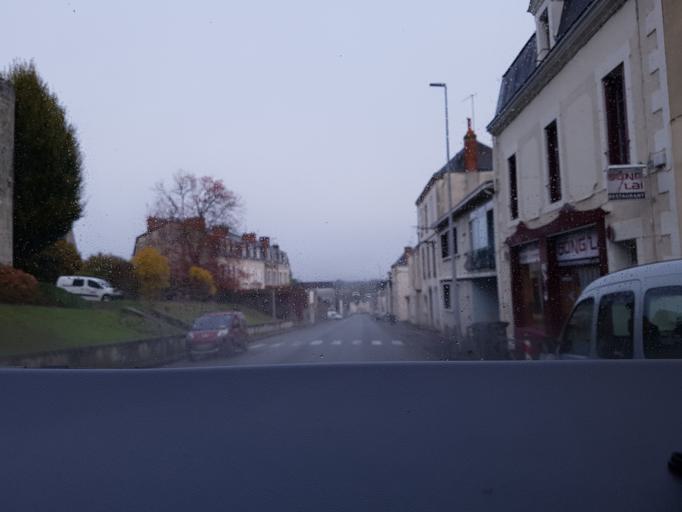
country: FR
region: Poitou-Charentes
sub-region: Departement des Deux-Sevres
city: Parthenay
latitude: 46.6488
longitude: -0.2467
